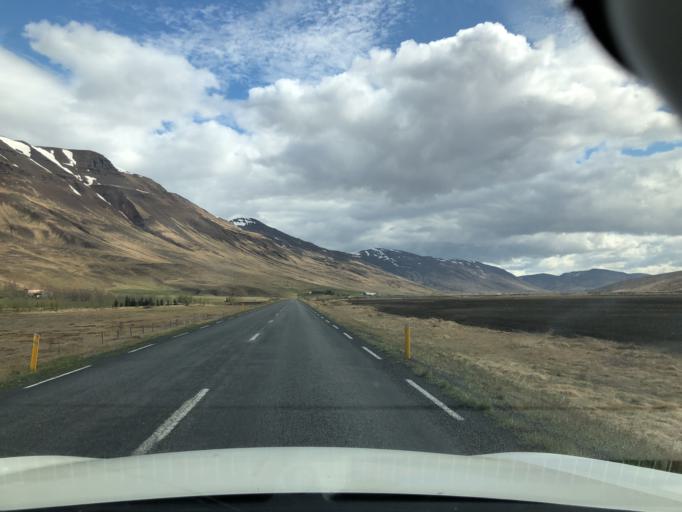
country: IS
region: Northwest
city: Saudarkrokur
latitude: 65.5772
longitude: -20.0236
